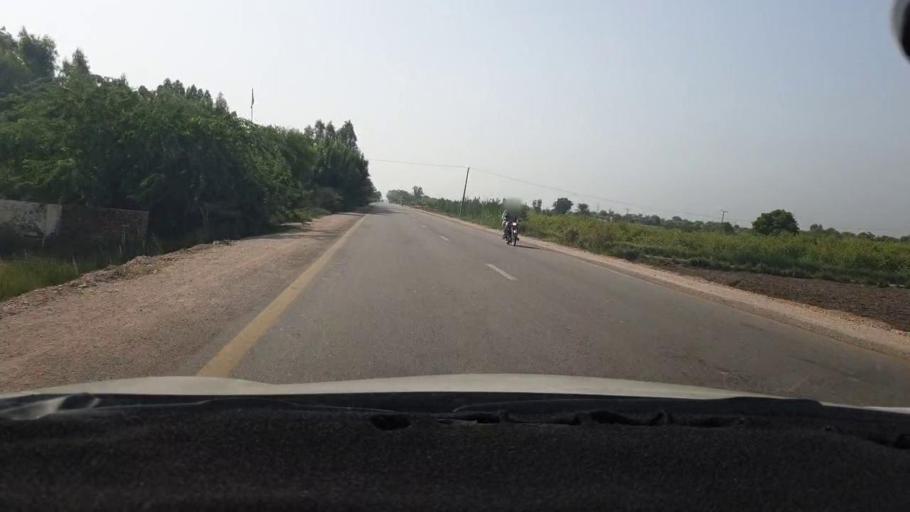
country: PK
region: Sindh
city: Sanghar
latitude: 26.0019
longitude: 68.9619
